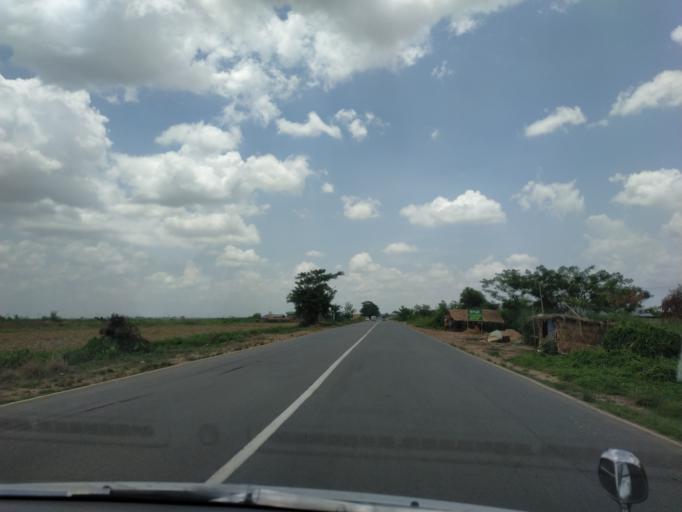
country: MM
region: Bago
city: Bago
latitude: 17.4703
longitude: 96.5561
